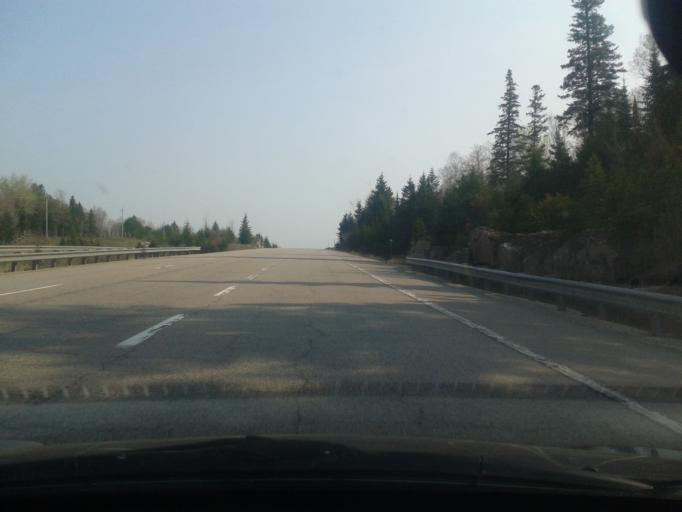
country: CA
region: Ontario
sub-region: Nipissing District
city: North Bay
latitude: 46.1999
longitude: -79.3531
